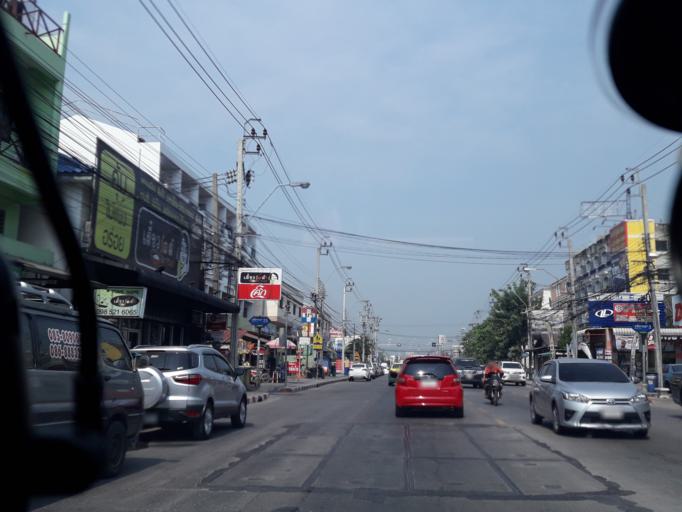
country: TH
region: Bangkok
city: Khlong Sam Wa
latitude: 13.8277
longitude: 100.7202
